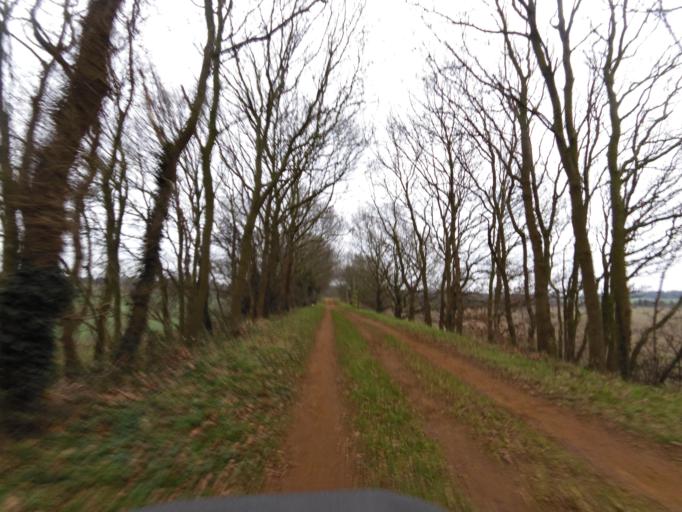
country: GB
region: England
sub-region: Norfolk
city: Costessey
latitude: 52.7117
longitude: 1.1572
